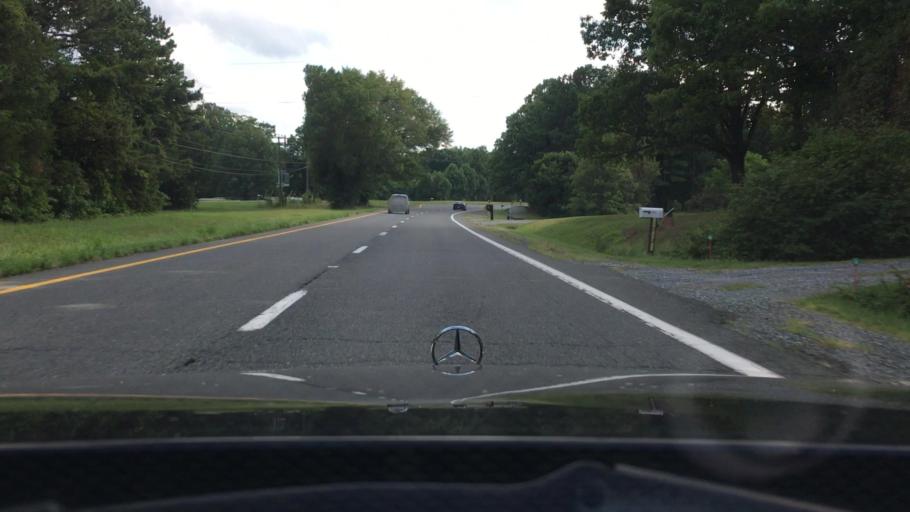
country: US
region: Virginia
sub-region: Campbell County
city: Altavista
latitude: 37.1612
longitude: -79.2216
